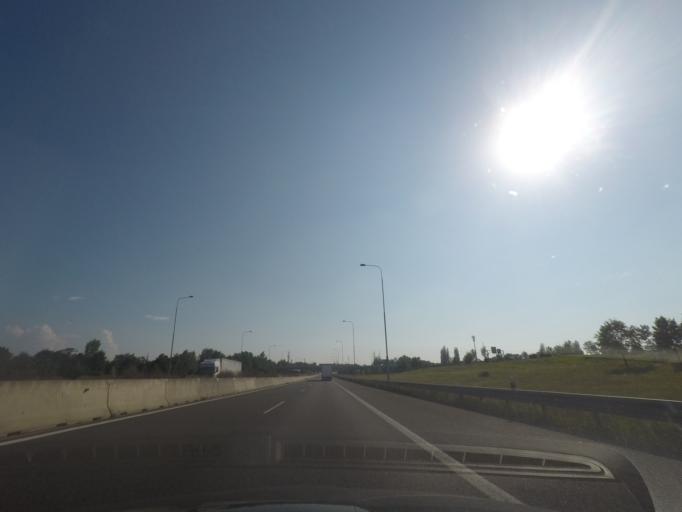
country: CZ
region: Moravskoslezsky
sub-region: Okres Ostrava-Mesto
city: Ostrava
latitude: 49.8572
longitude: 18.2551
